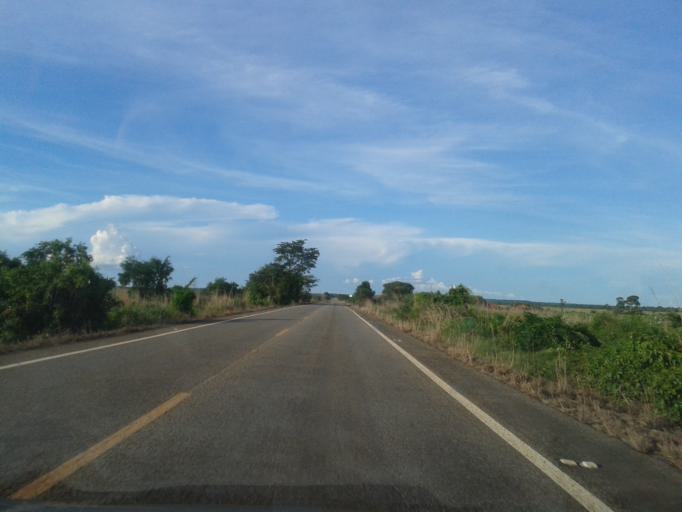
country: BR
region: Goias
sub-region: Sao Miguel Do Araguaia
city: Sao Miguel do Araguaia
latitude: -13.6010
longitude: -50.3195
